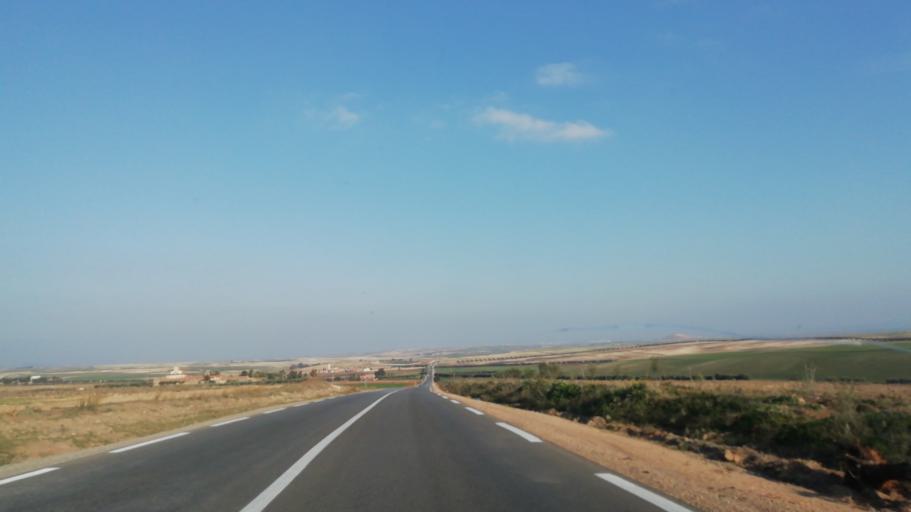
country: DZ
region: Sidi Bel Abbes
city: Sidi Bel Abbes
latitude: 35.1737
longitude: -0.8301
